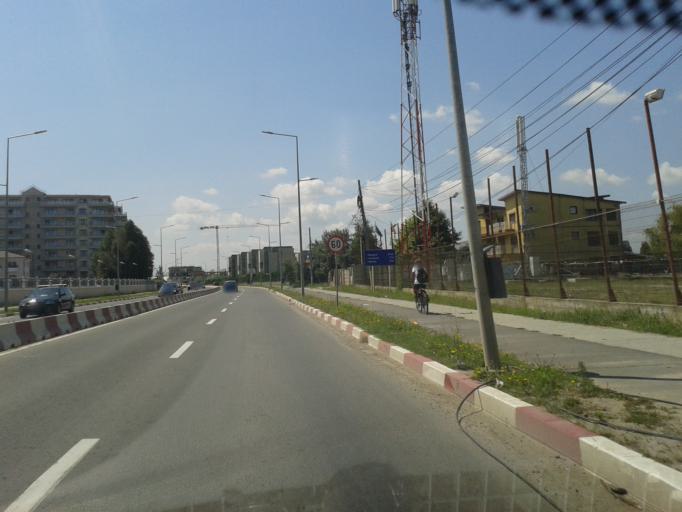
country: RO
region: Constanta
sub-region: Comuna Navodari
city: Navodari
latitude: 44.2809
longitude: 28.6178
